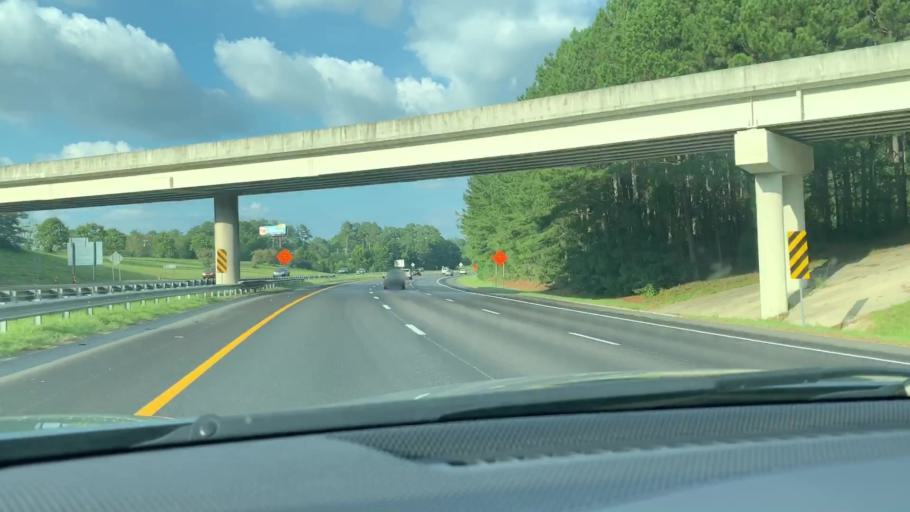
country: US
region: South Carolina
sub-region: Richland County
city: Woodfield
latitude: 34.0407
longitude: -80.9367
